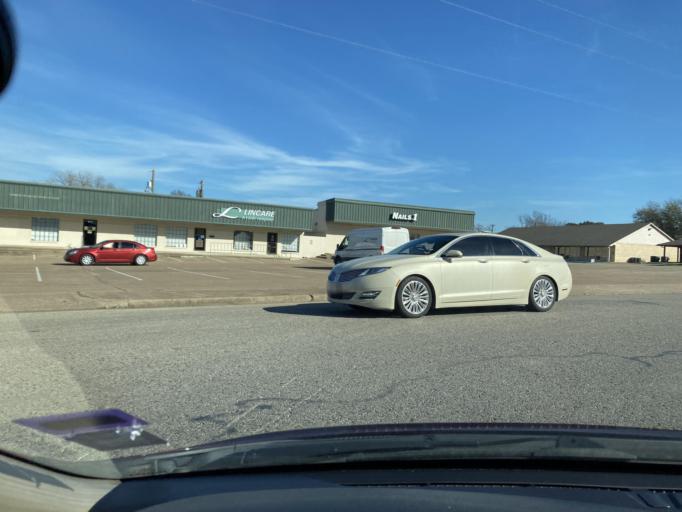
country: US
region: Texas
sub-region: Navarro County
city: Corsicana
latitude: 32.1002
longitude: -96.4698
